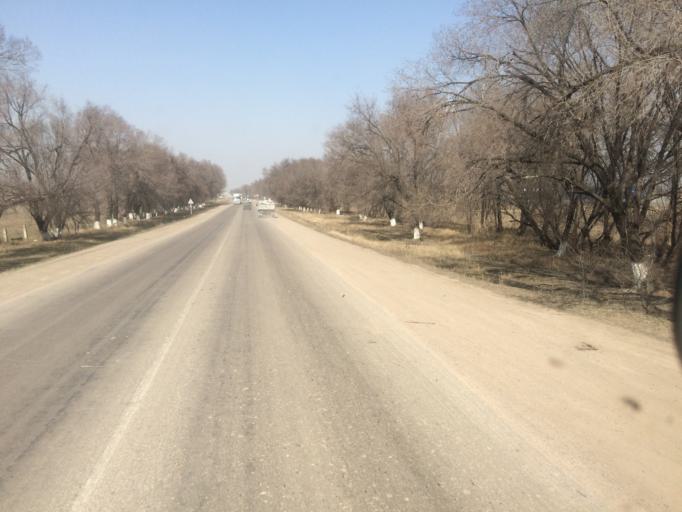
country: KZ
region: Almaty Oblysy
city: Burunday
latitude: 43.3273
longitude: 76.6624
